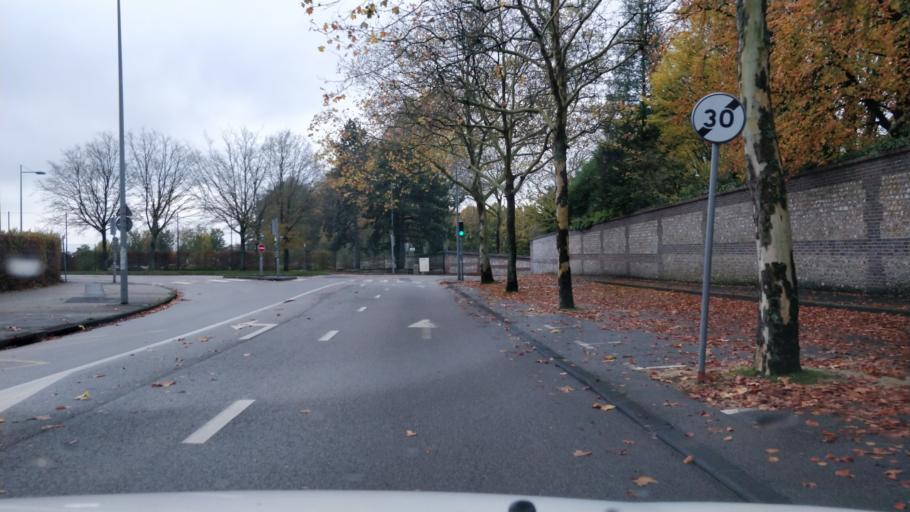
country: FR
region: Haute-Normandie
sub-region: Departement de la Seine-Maritime
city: Bihorel
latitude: 49.4506
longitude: 1.1207
